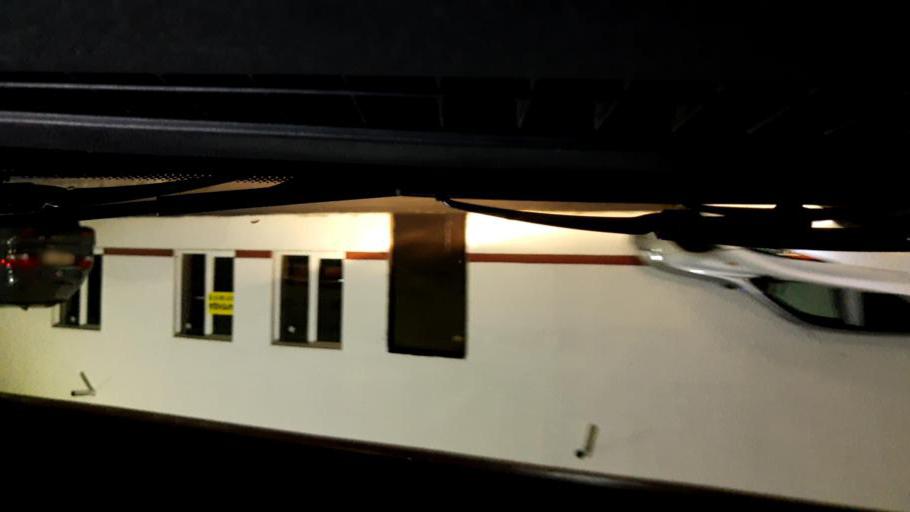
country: RU
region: Bashkortostan
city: Mikhaylovka
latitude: 54.7888
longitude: 55.8693
